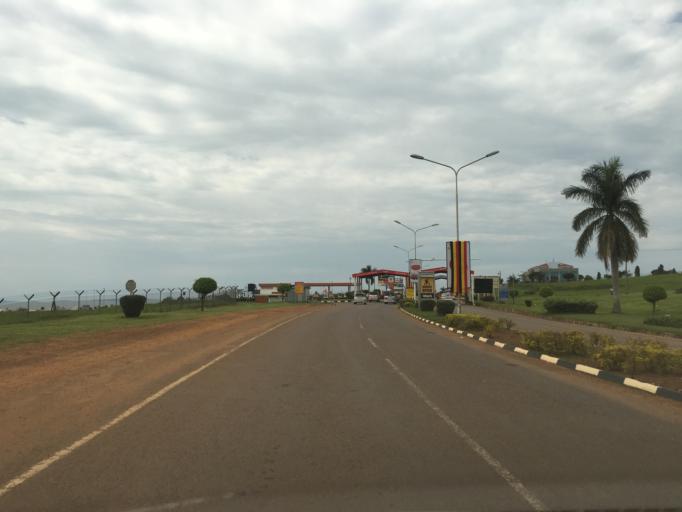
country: UG
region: Central Region
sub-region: Wakiso District
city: Entebbe
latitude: 0.0436
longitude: 32.4474
